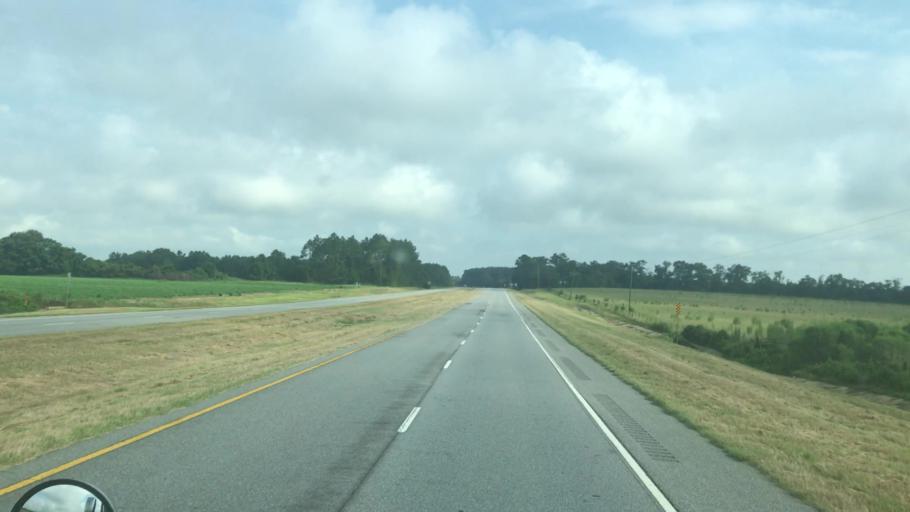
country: US
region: Georgia
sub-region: Miller County
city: Colquitt
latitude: 31.2191
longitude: -84.7786
